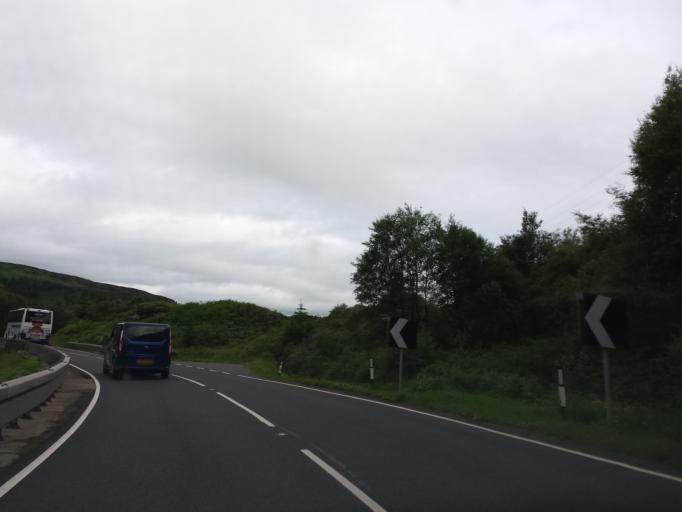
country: GB
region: Scotland
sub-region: Stirling
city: Callander
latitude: 56.4176
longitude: -4.3297
